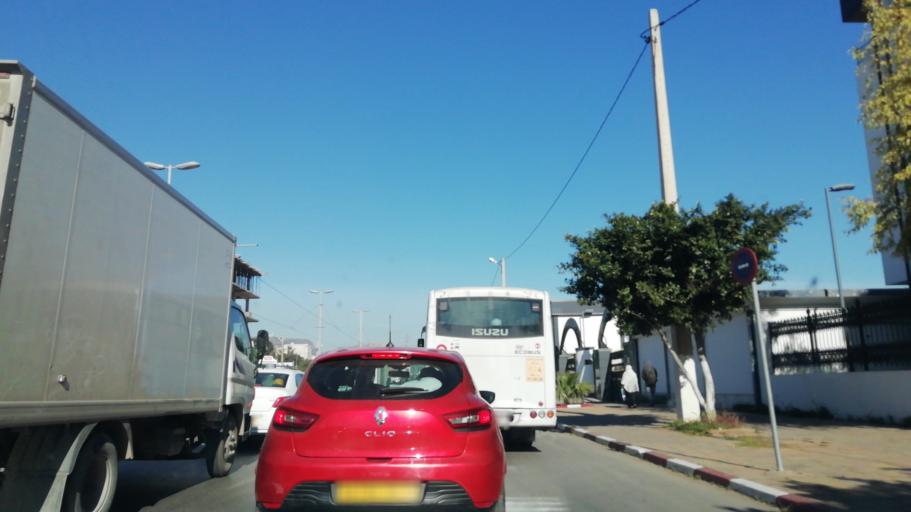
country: DZ
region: Oran
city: Oran
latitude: 35.6779
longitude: -0.6421
